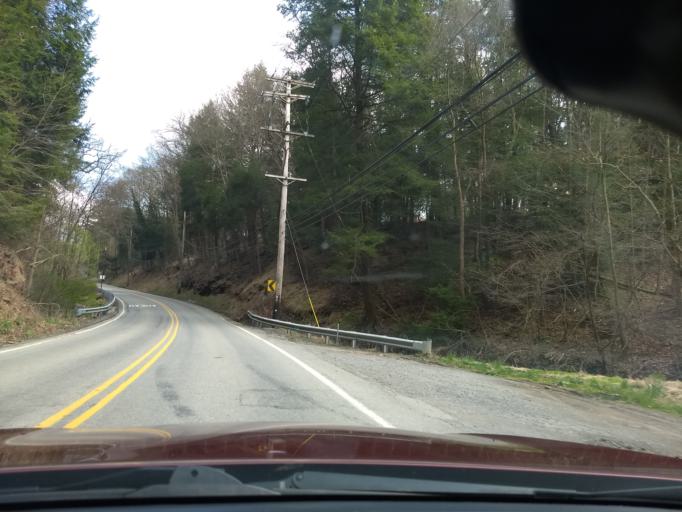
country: US
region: Pennsylvania
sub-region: Allegheny County
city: Allison Park
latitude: 40.5664
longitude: -79.9351
